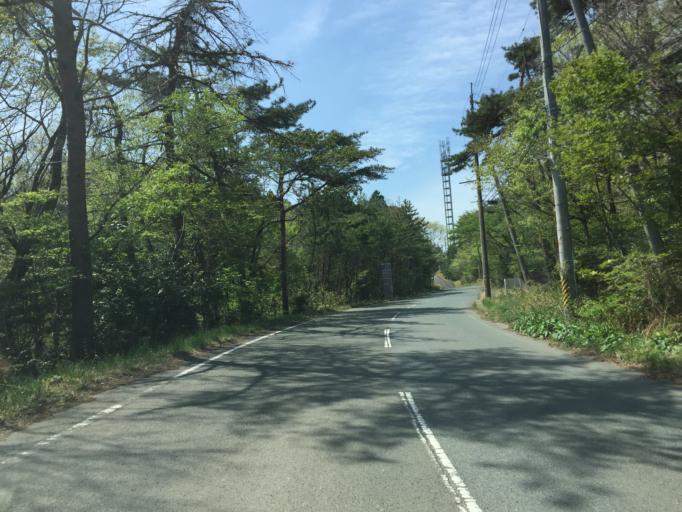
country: JP
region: Miyagi
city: Marumori
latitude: 37.9002
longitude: 140.9037
